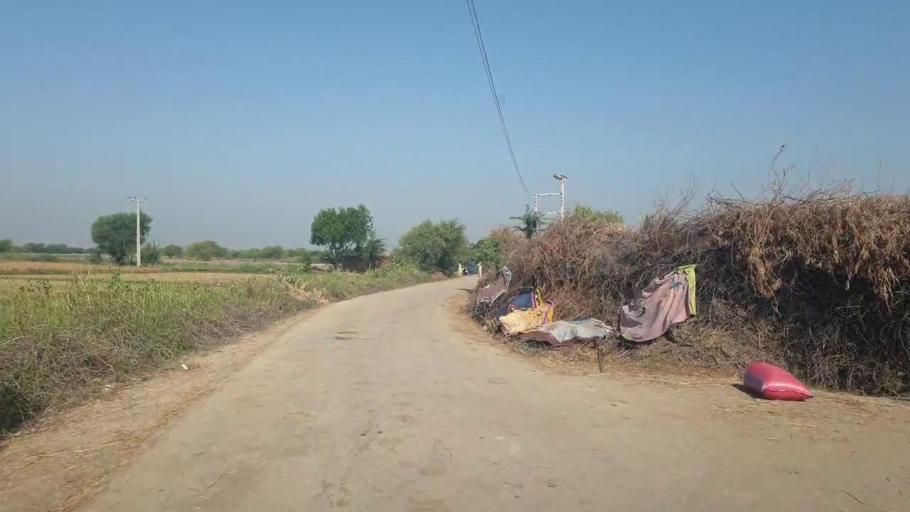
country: PK
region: Sindh
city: Tando Bago
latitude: 24.7348
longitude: 68.8924
